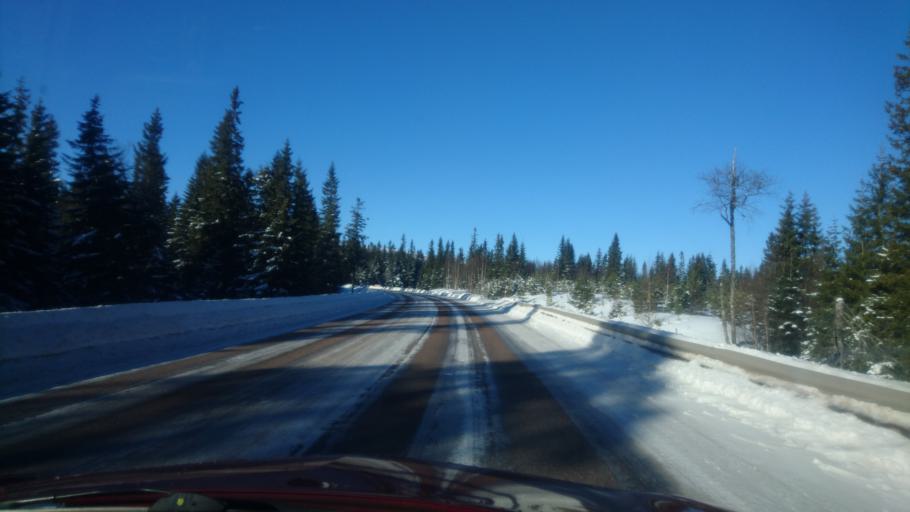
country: SE
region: Dalarna
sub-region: Malung-Saelens kommun
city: Malung
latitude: 61.1684
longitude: 13.1906
